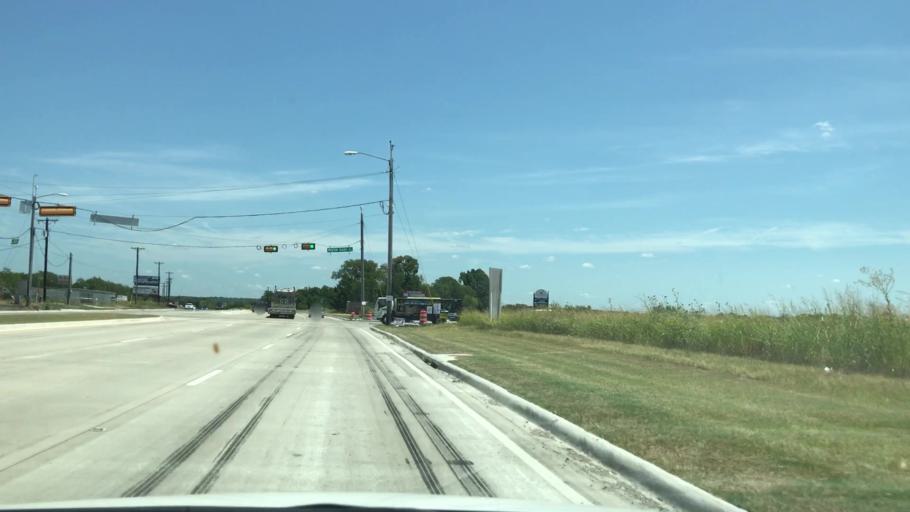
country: US
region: Texas
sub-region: Collin County
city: Wylie
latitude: 33.0228
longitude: -96.4967
